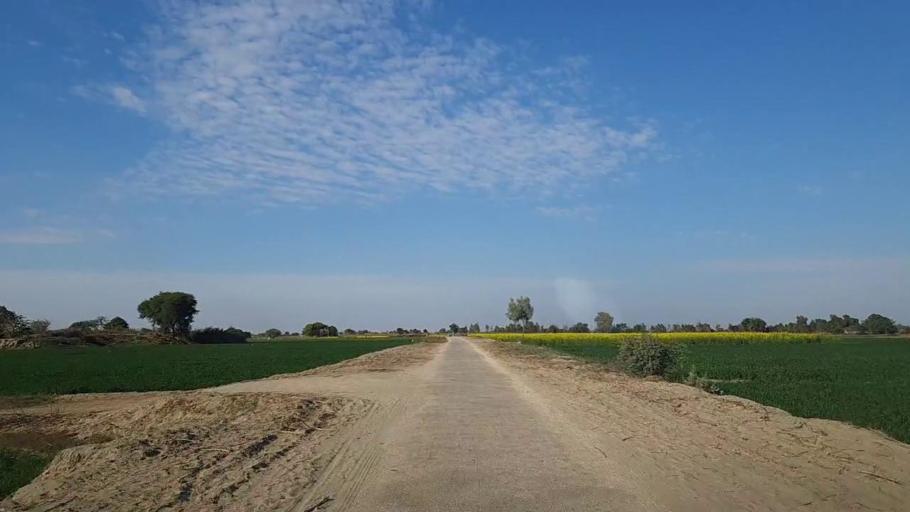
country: PK
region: Sindh
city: Khadro
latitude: 26.3050
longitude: 68.8343
